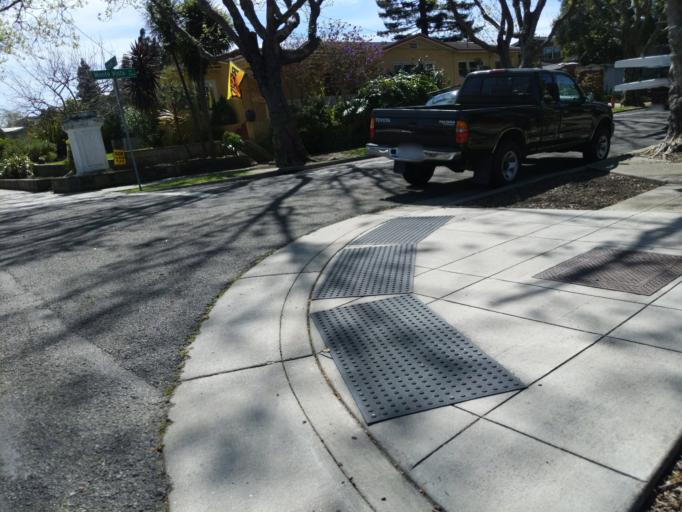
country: US
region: California
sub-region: Alameda County
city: Alameda
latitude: 37.7613
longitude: -122.2256
